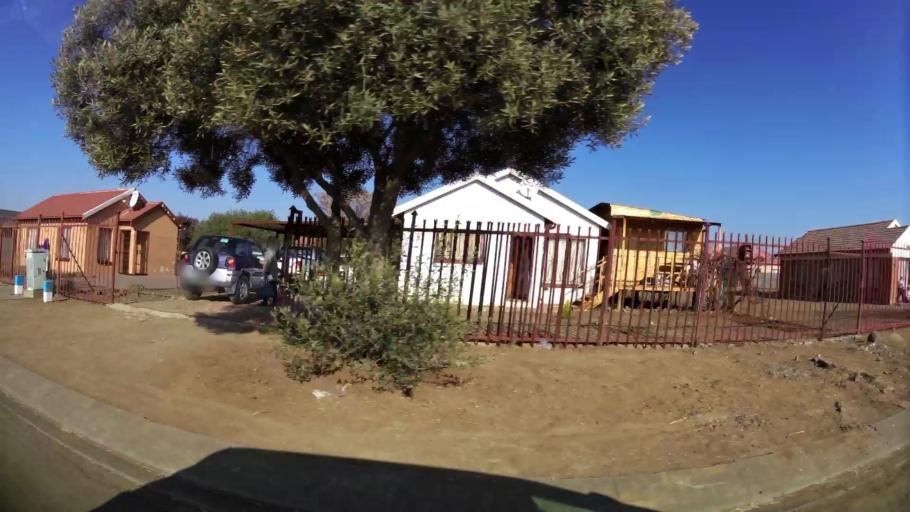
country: ZA
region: Orange Free State
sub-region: Mangaung Metropolitan Municipality
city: Bloemfontein
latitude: -29.1824
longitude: 26.1755
